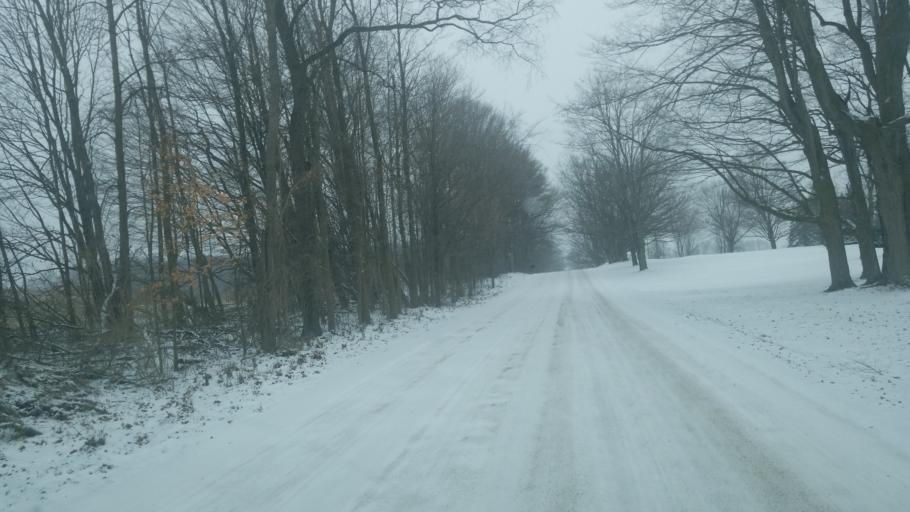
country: US
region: Michigan
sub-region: Osceola County
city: Reed City
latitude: 43.8396
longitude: -85.3940
